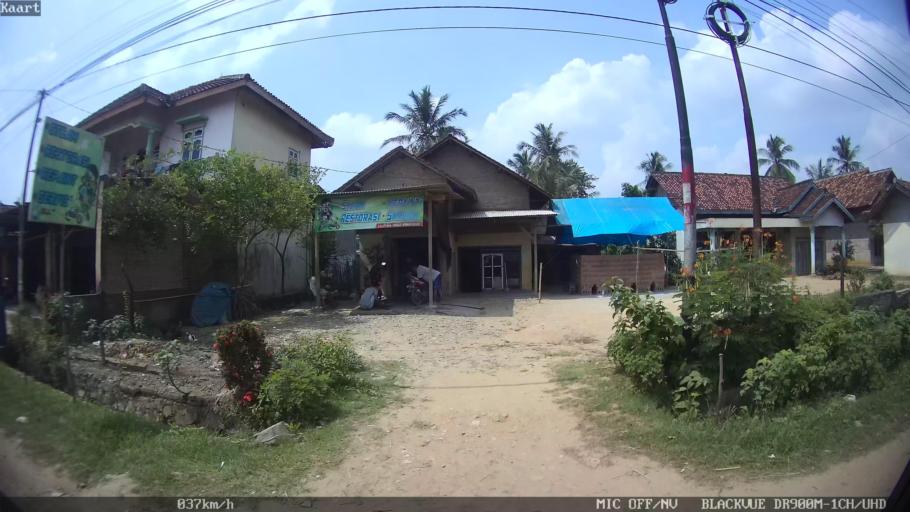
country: ID
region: Lampung
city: Pringsewu
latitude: -5.3871
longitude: 104.9655
